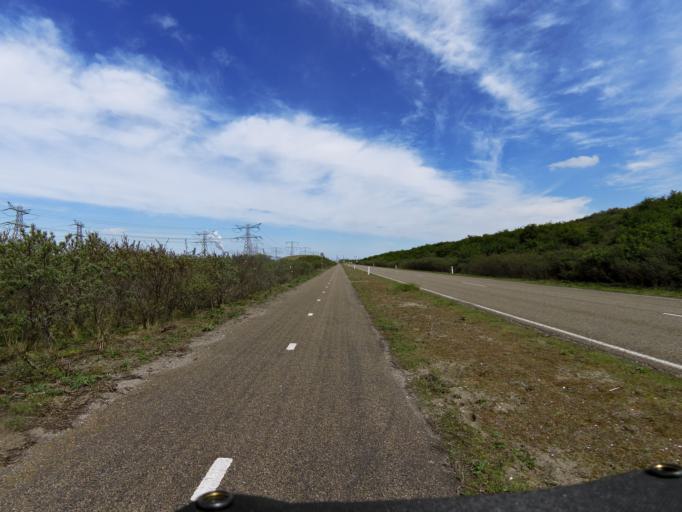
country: NL
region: South Holland
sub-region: Gemeente Rotterdam
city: Hoek van Holland
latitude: 51.9250
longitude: 4.0336
